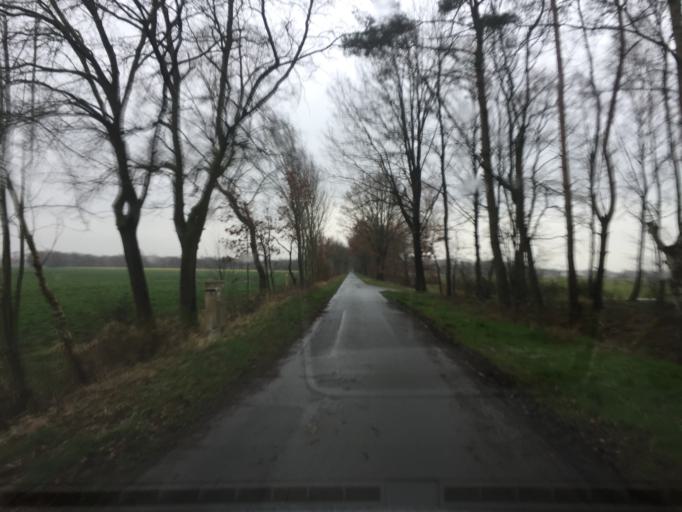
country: DE
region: Lower Saxony
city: Borstel
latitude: 52.6177
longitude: 8.9105
